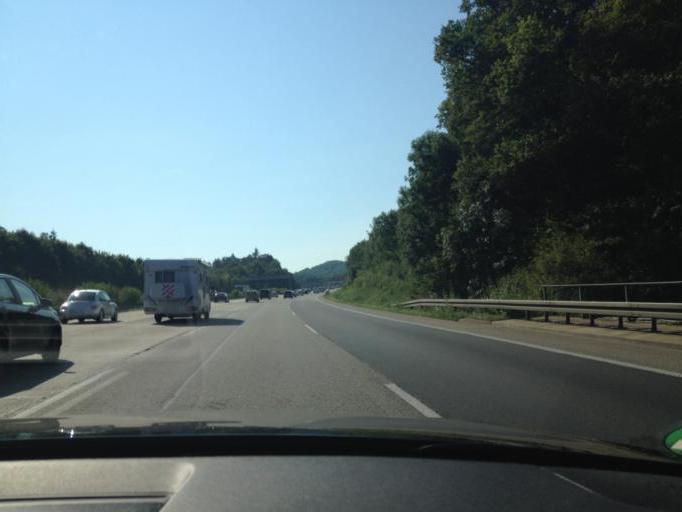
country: DE
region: Baden-Wuerttemberg
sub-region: Regierungsbezirk Stuttgart
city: Leonberg
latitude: 48.7726
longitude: 9.0274
